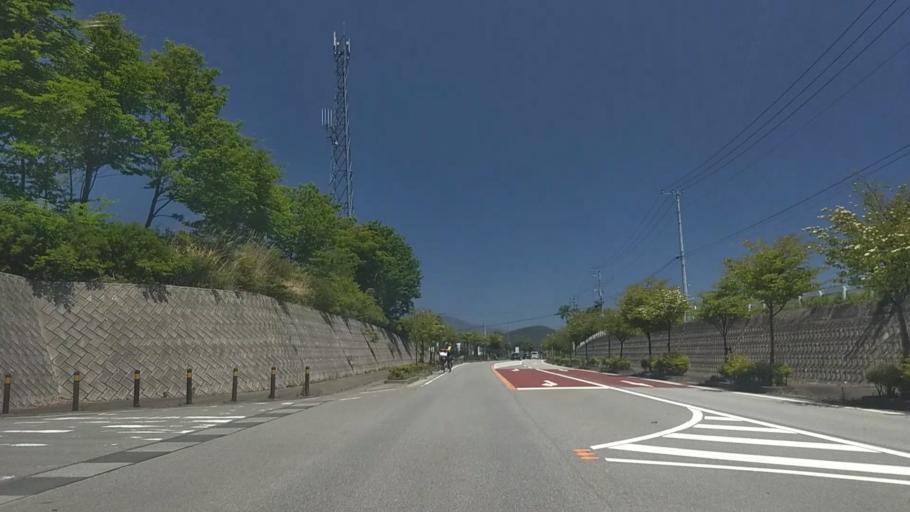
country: JP
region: Yamanashi
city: Nirasaki
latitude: 35.8219
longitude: 138.4288
